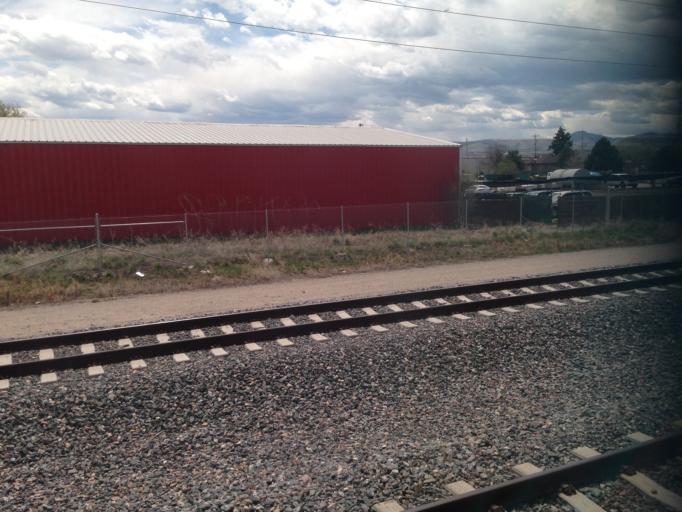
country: US
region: Colorado
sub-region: Jefferson County
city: Arvada
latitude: 39.7887
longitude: -105.1296
